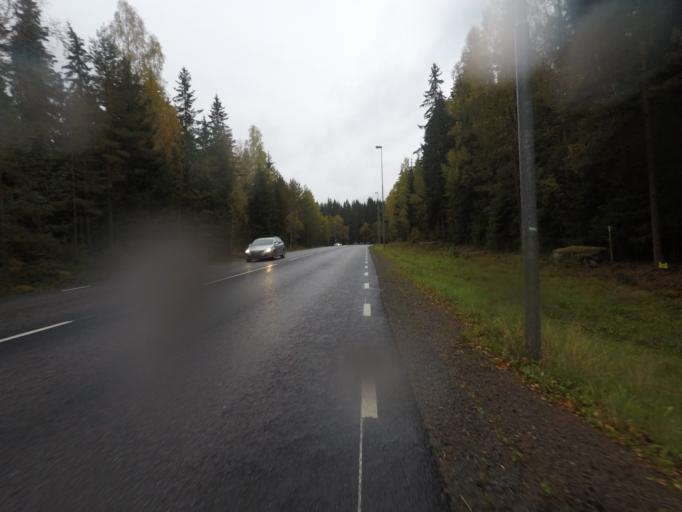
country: SE
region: OErebro
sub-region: Karlskoga Kommun
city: Karlskoga
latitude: 59.3081
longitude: 14.4674
